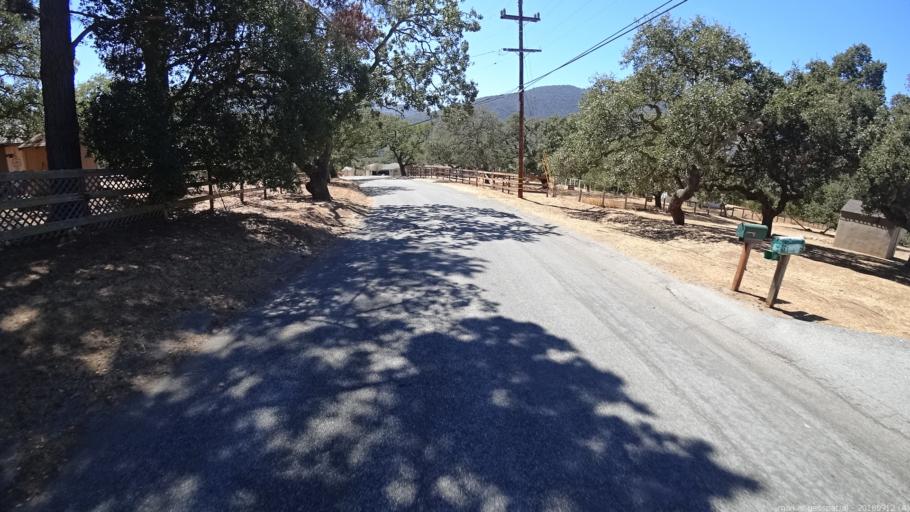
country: US
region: California
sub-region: Monterey County
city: Carmel Valley Village
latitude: 36.4999
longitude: -121.7474
